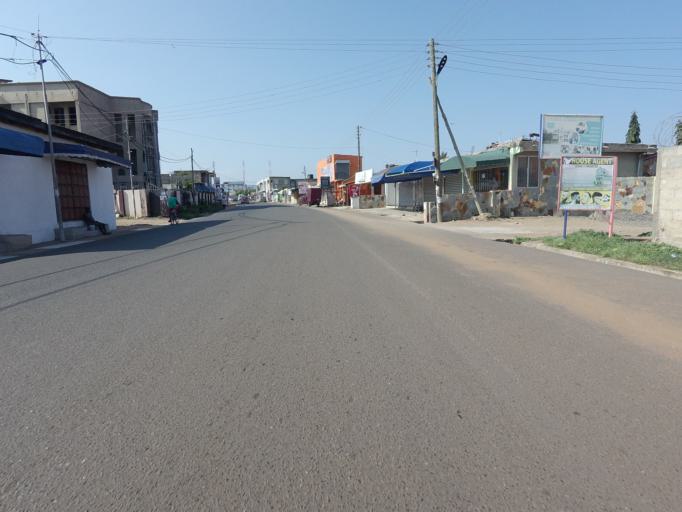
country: GH
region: Greater Accra
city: Nungua
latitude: 5.6252
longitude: -0.0908
